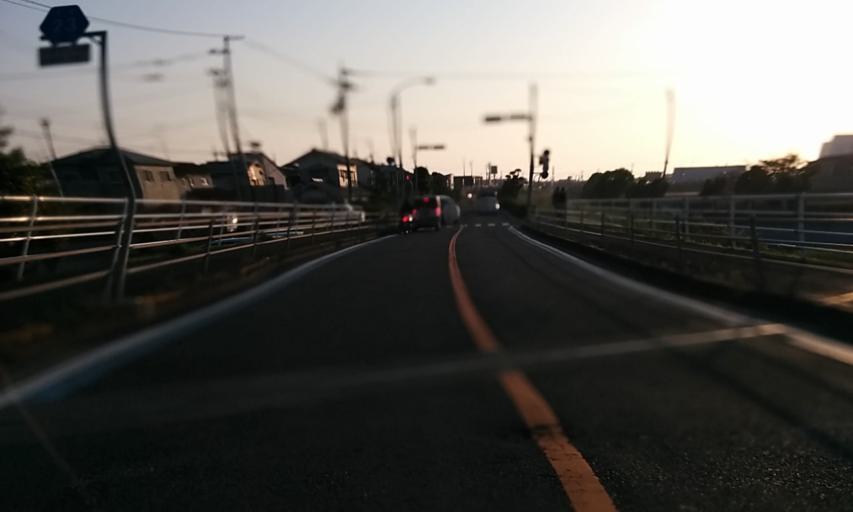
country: JP
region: Ehime
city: Masaki-cho
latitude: 33.7704
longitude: 132.7138
